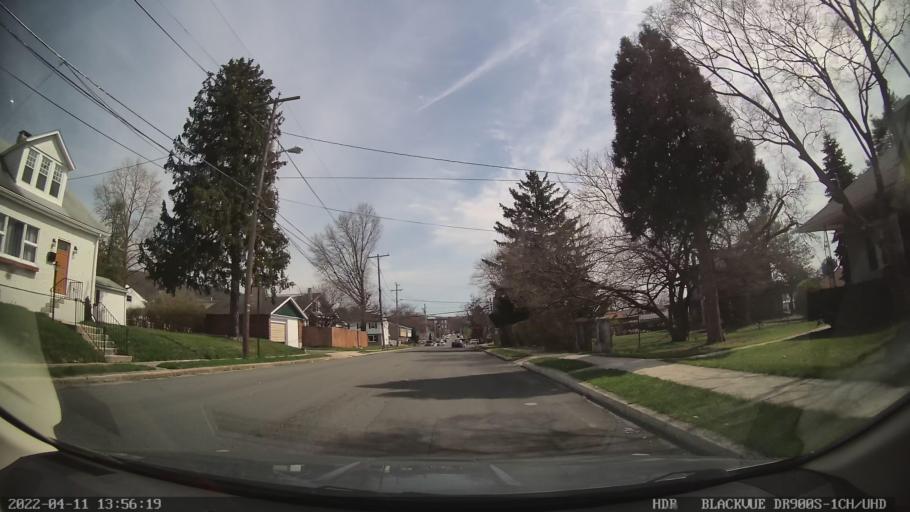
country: US
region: Pennsylvania
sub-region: Berks County
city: Laureldale
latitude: 40.3910
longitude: -75.9110
